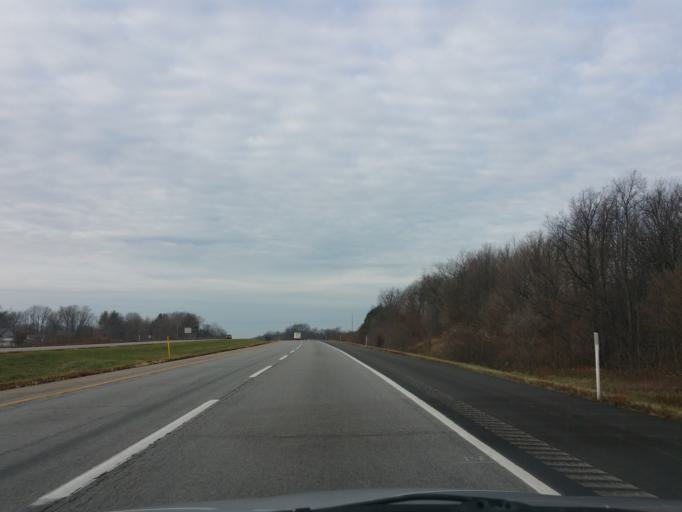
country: US
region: Indiana
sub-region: LaPorte County
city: LaPorte
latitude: 41.6746
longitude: -86.6940
